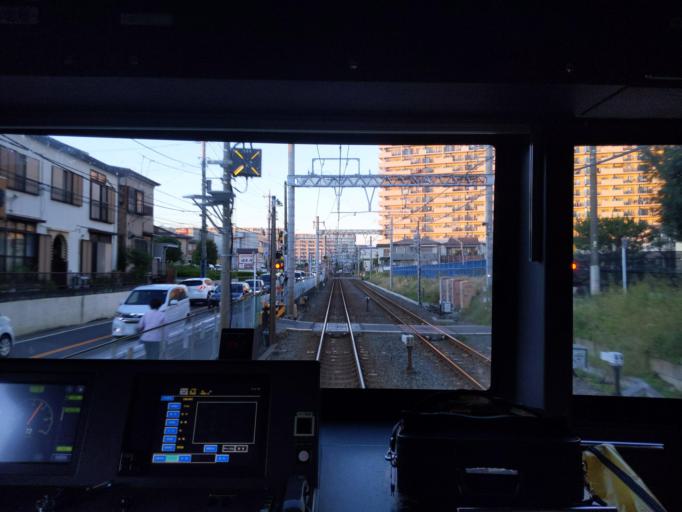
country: JP
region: Chiba
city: Funabashi
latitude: 35.7164
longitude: 139.9805
